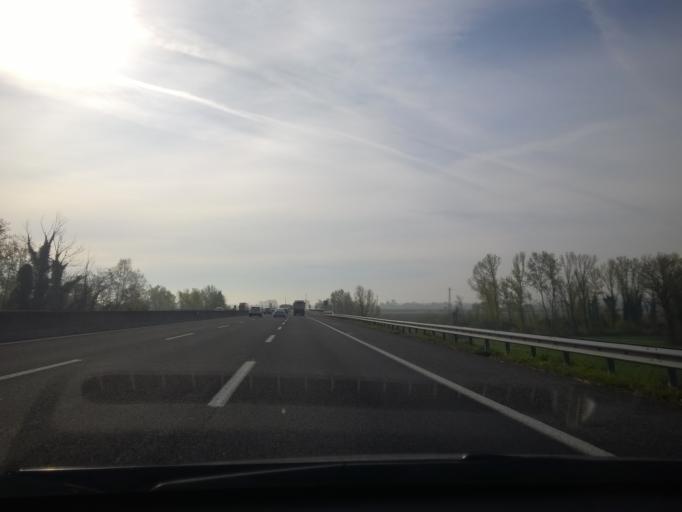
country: IT
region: Emilia-Romagna
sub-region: Provincia di Bologna
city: Toscanella
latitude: 44.4177
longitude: 11.6247
